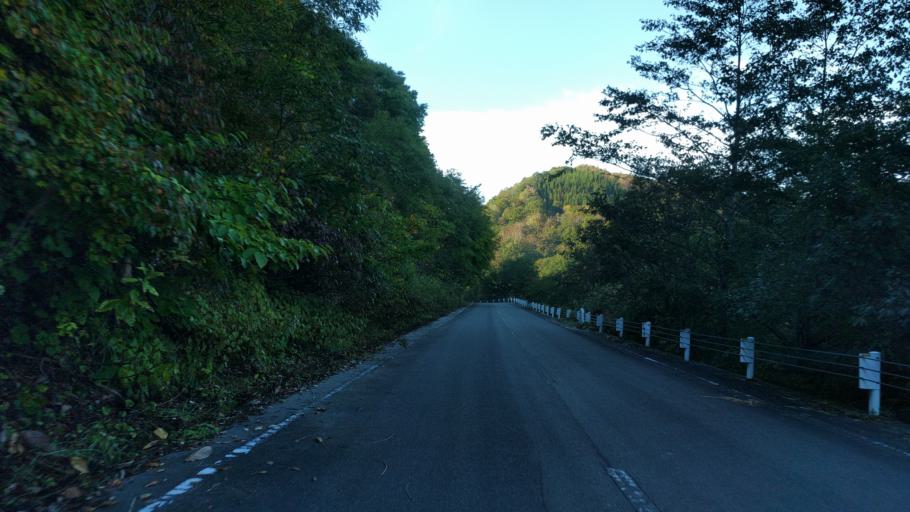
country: JP
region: Fukushima
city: Kitakata
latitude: 37.4022
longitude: 139.7614
